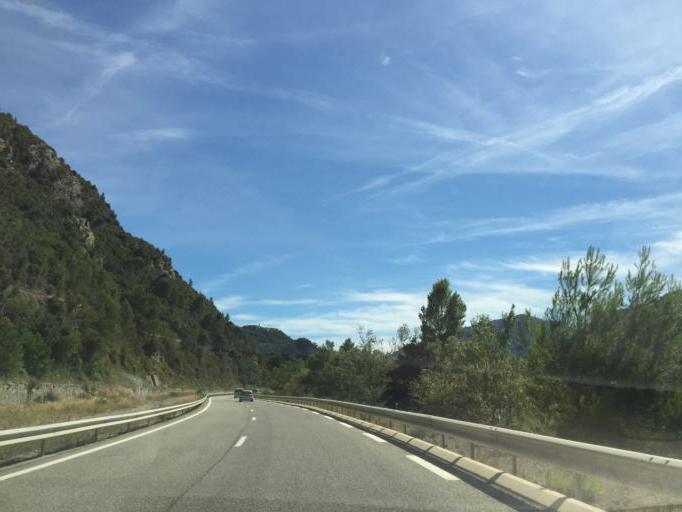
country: FR
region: Provence-Alpes-Cote d'Azur
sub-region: Departement des Alpes-Maritimes
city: Levens
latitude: 43.8538
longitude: 7.1978
